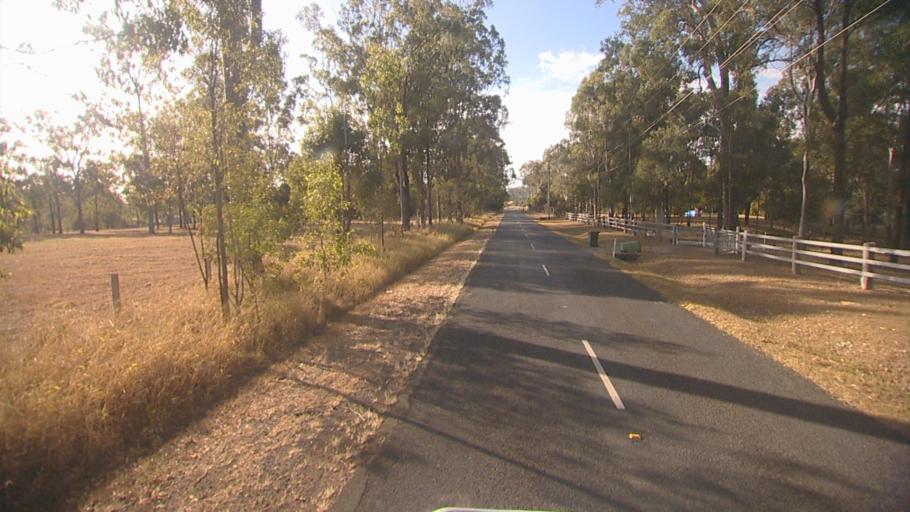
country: AU
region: Queensland
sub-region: Logan
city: Cedar Vale
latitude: -27.8693
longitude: 153.0111
